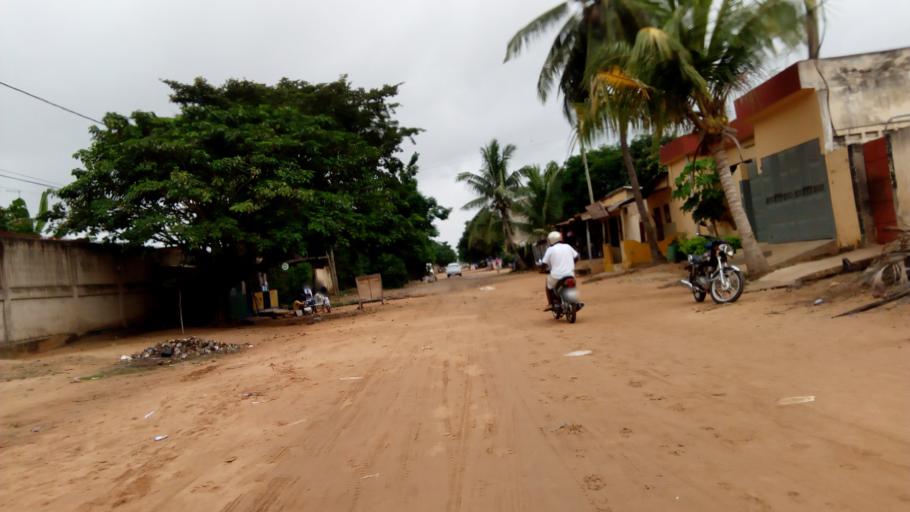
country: TG
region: Maritime
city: Lome
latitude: 6.1792
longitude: 1.1776
